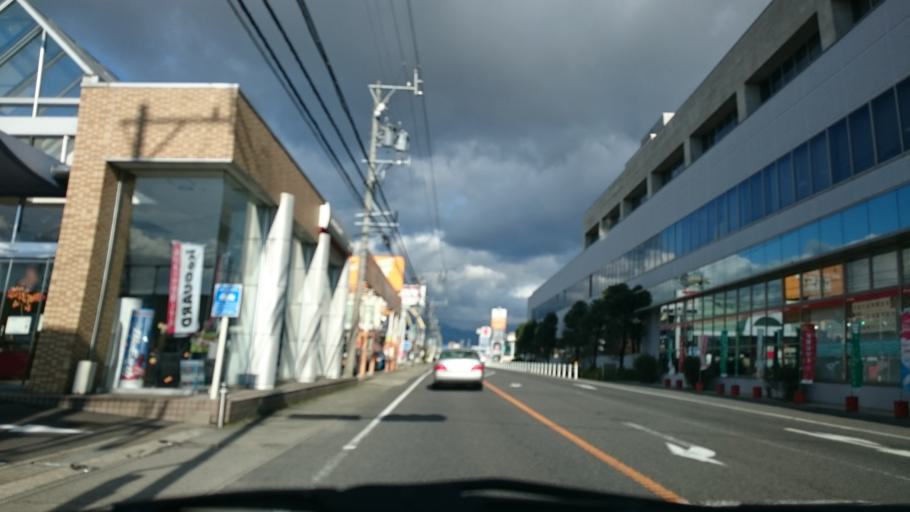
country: JP
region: Mie
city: Komono
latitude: 34.9926
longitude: 136.5473
